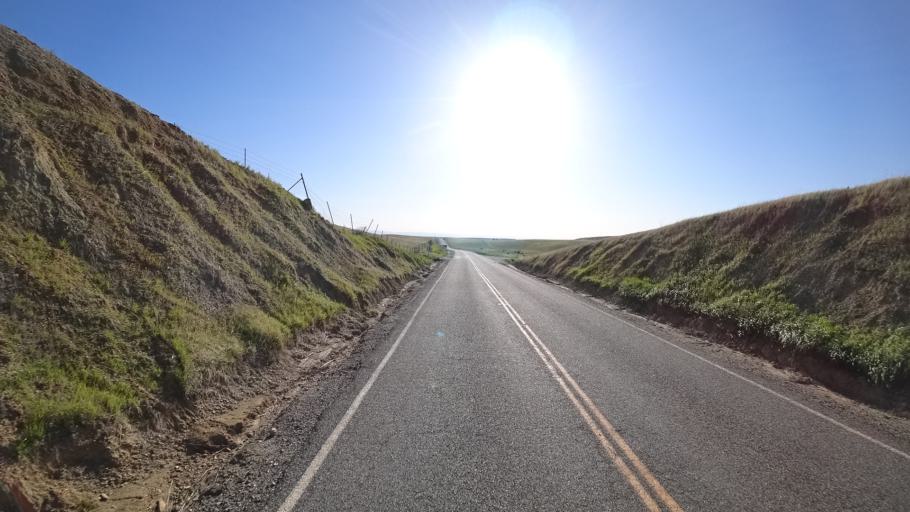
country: US
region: California
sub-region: Glenn County
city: Orland
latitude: 39.8288
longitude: -122.3662
